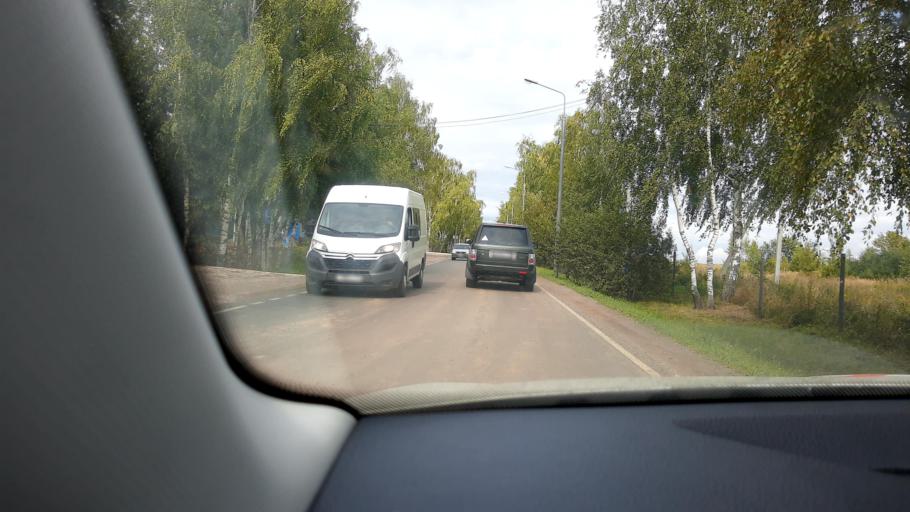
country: RU
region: Moskovskaya
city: Annino
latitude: 55.5679
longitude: 37.2356
